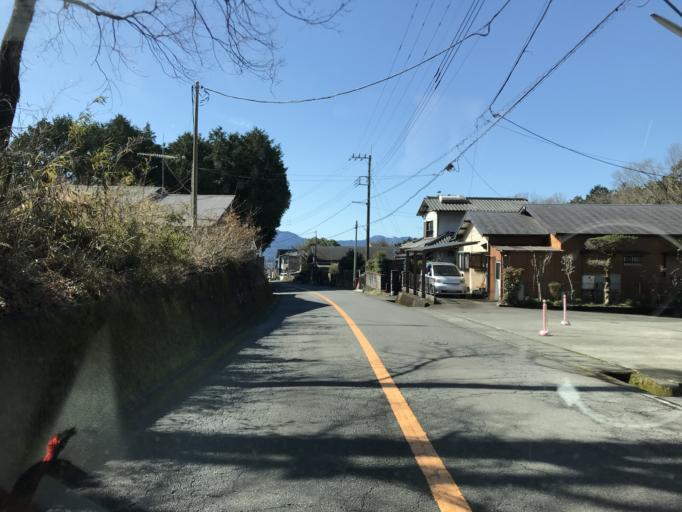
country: JP
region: Shizuoka
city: Fujinomiya
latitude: 35.2299
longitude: 138.6504
